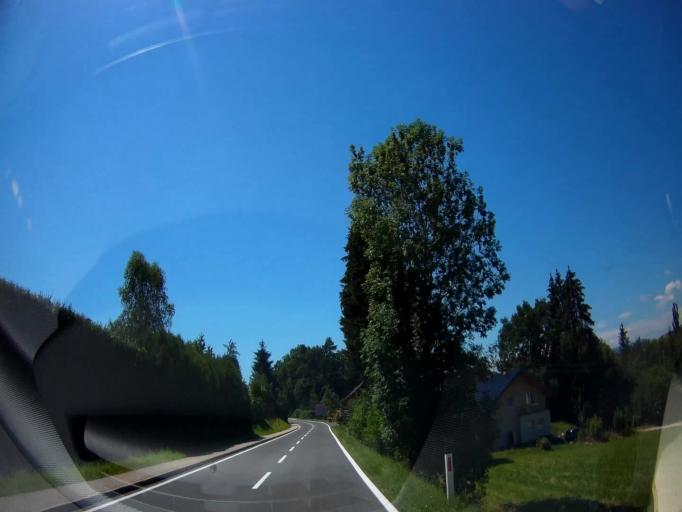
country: AT
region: Carinthia
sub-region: Politischer Bezirk Volkermarkt
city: Eberndorf
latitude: 46.6132
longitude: 14.5797
